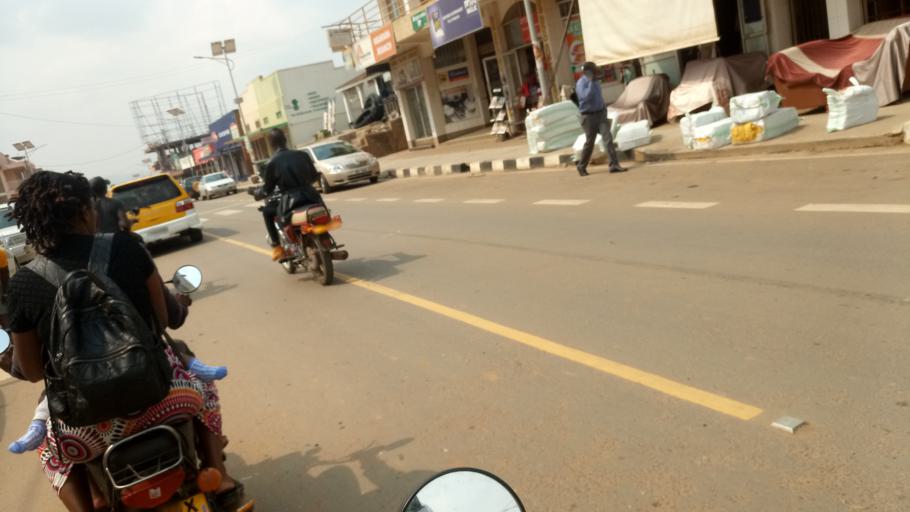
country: UG
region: Western Region
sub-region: Mbarara District
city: Mbarara
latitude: -0.6064
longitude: 30.6608
